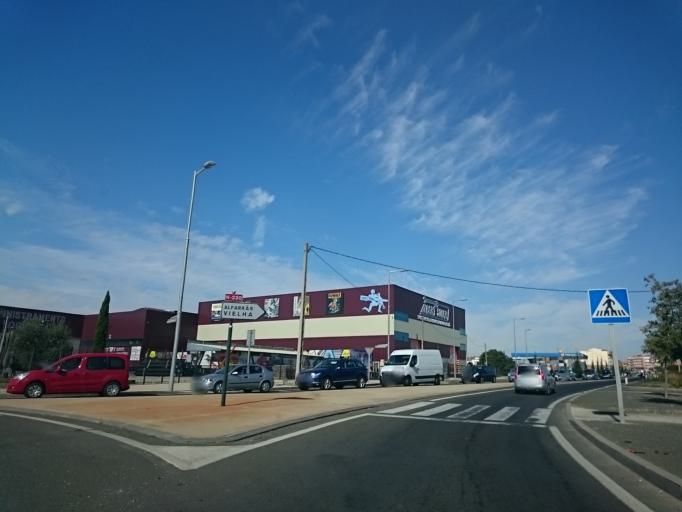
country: ES
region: Catalonia
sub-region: Provincia de Lleida
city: Torrefarrera
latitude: 41.6700
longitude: 0.6057
